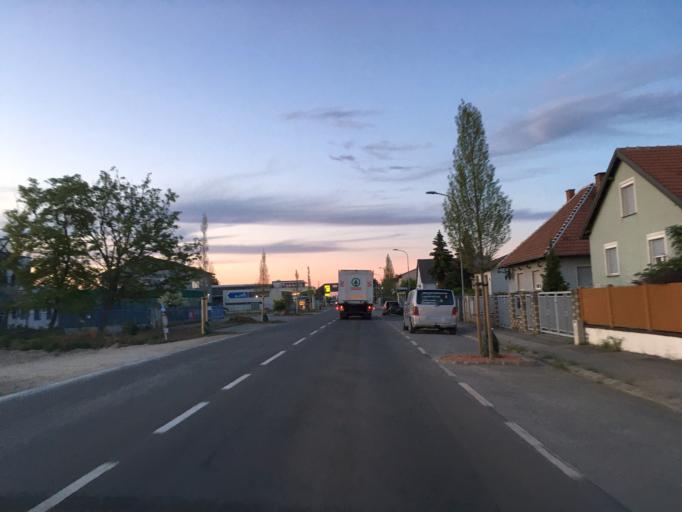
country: AT
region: Lower Austria
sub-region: Politischer Bezirk Wien-Umgebung
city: Zwolfaxing
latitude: 48.1147
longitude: 16.4658
